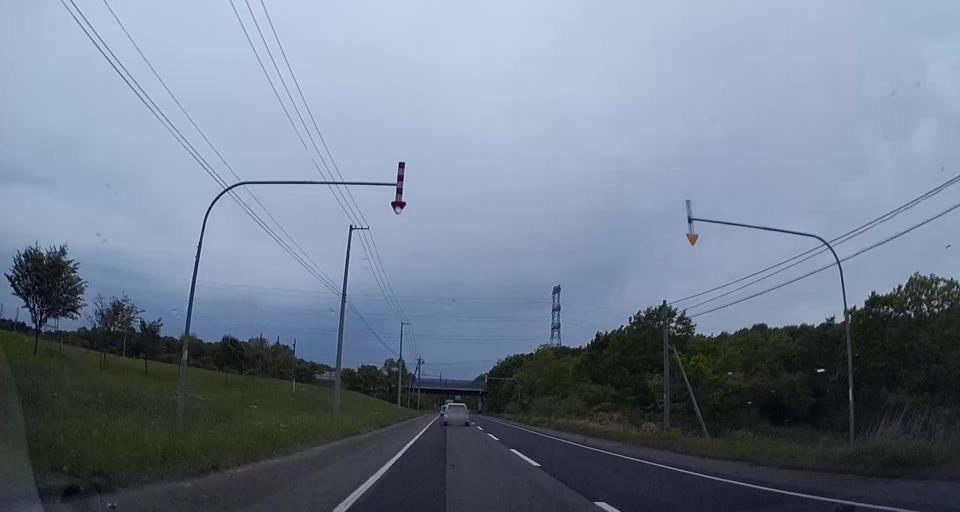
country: JP
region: Hokkaido
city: Chitose
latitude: 42.7109
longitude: 141.7484
